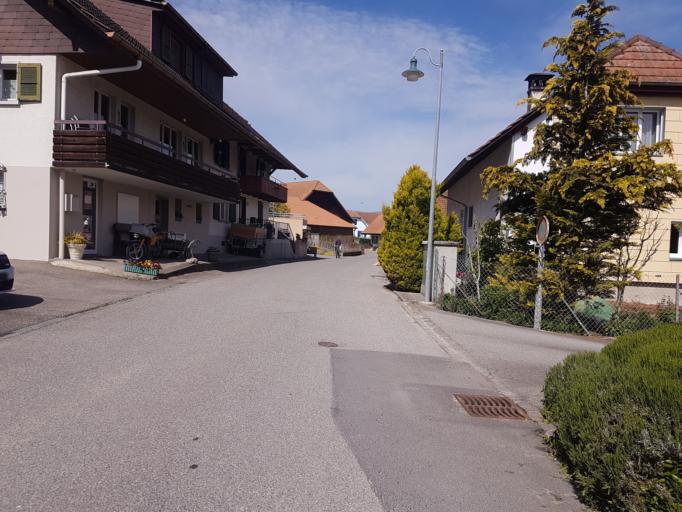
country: CH
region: Bern
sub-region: Seeland District
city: Tauffelen
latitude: 47.0466
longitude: 7.1533
